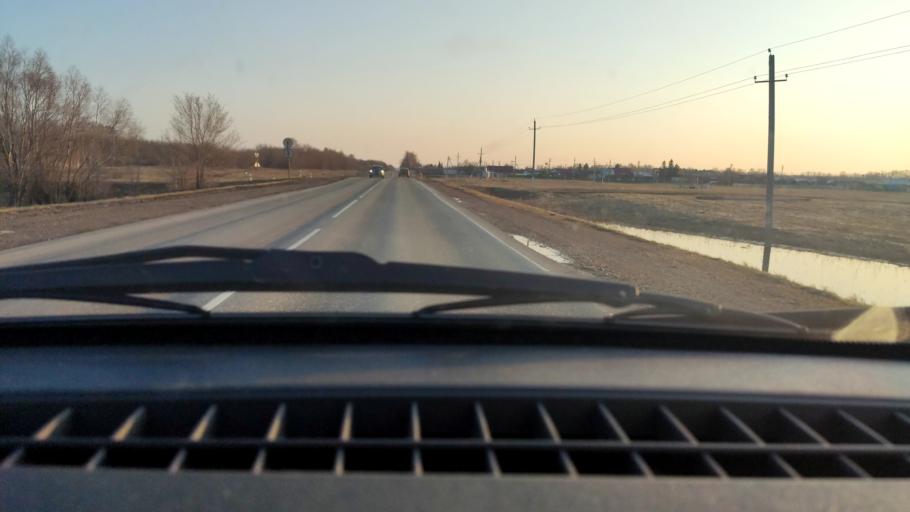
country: RU
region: Bashkortostan
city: Davlekanovo
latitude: 54.3030
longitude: 55.1349
